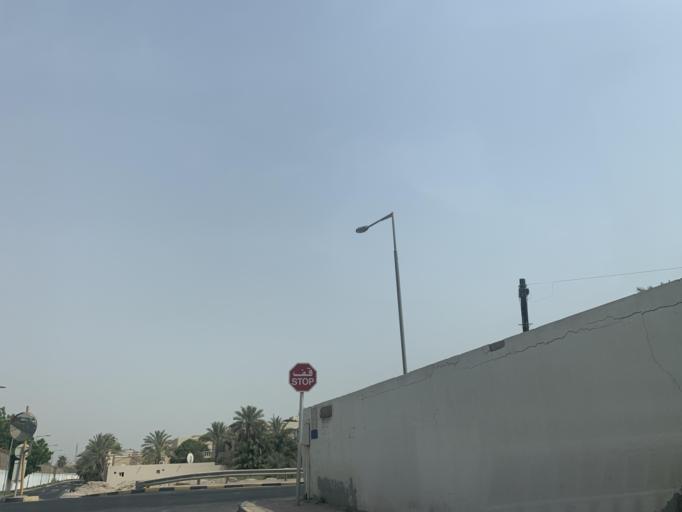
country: BH
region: Northern
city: Madinat `Isa
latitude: 26.1956
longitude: 50.4702
